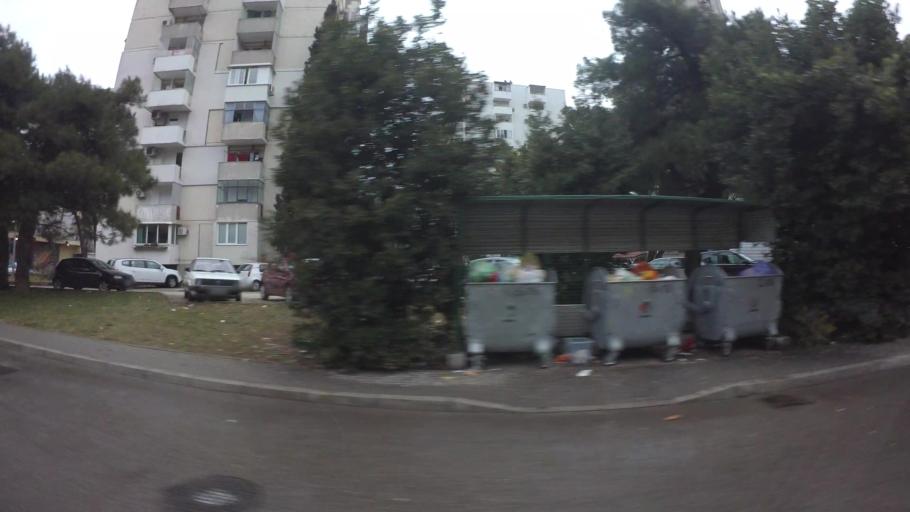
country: BA
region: Federation of Bosnia and Herzegovina
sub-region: Hercegovacko-Bosanski Kanton
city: Mostar
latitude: 43.3375
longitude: 17.8081
